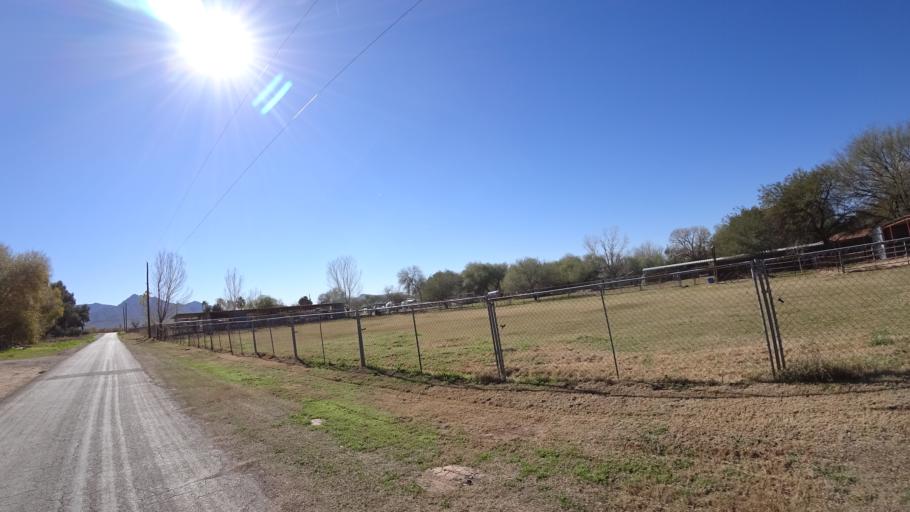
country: US
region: Arizona
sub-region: Maricopa County
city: Avondale
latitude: 33.3936
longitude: -112.3362
